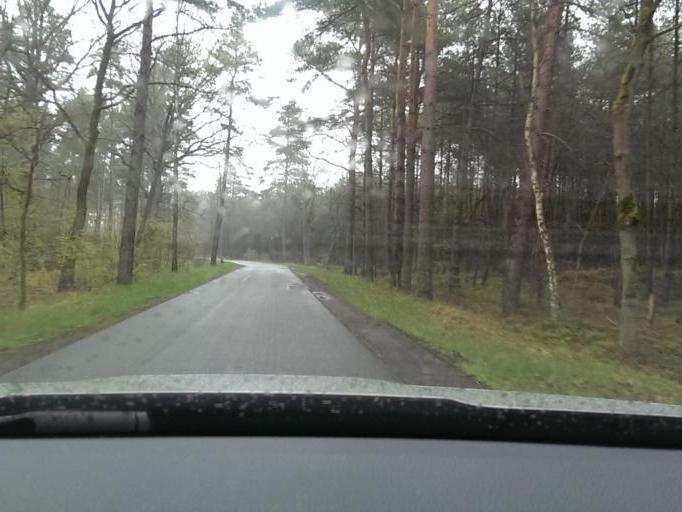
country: DE
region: Lower Saxony
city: Elze
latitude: 52.6043
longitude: 9.7780
